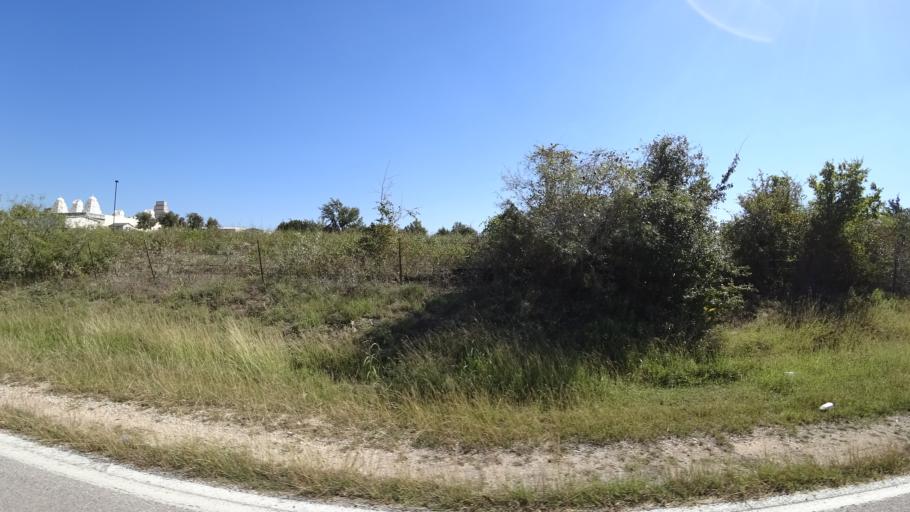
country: US
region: Texas
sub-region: Travis County
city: Hornsby Bend
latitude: 30.2804
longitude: -97.6199
